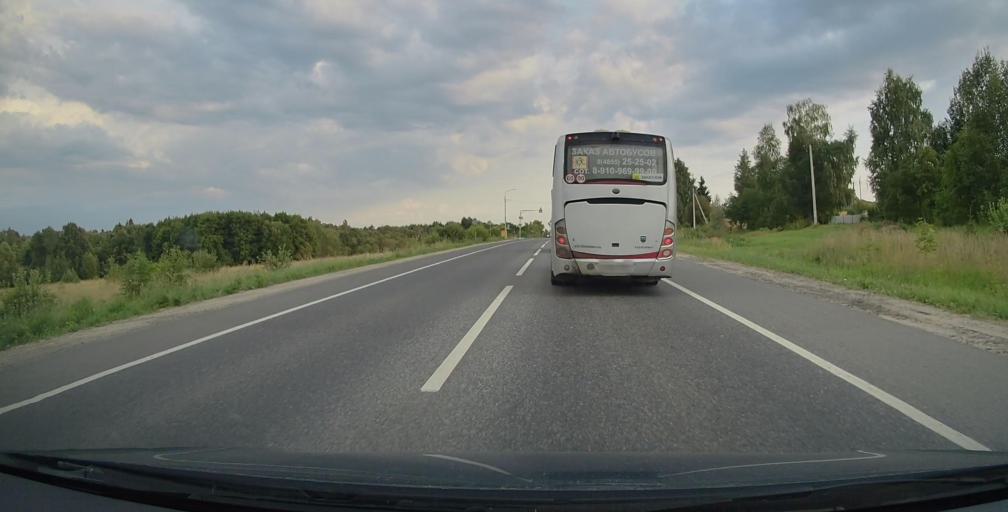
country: RU
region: Moskovskaya
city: Skoropuskovskiy
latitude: 56.3882
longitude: 38.1084
